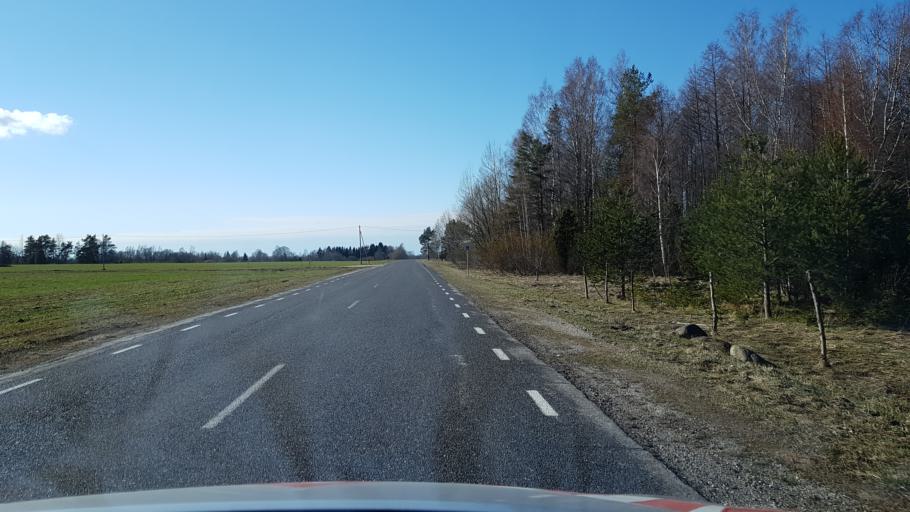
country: EE
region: Laeaene-Virumaa
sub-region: Kadrina vald
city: Kadrina
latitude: 59.5283
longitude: 26.0700
